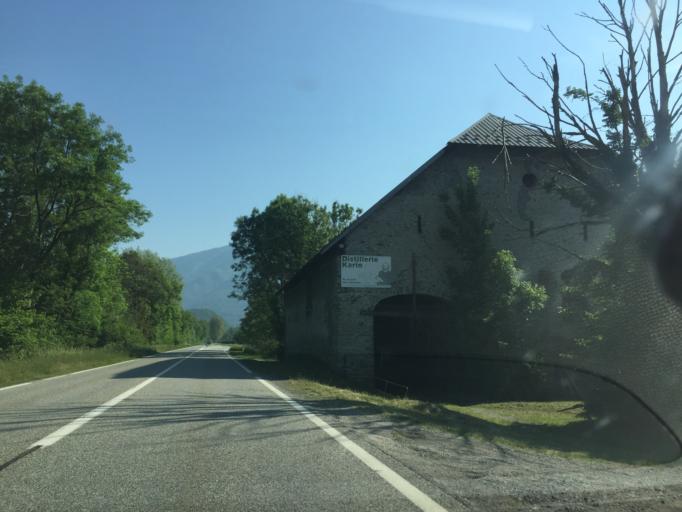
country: FR
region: Rhone-Alpes
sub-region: Departement de la Savoie
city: Aiton
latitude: 45.4865
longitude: 6.2952
